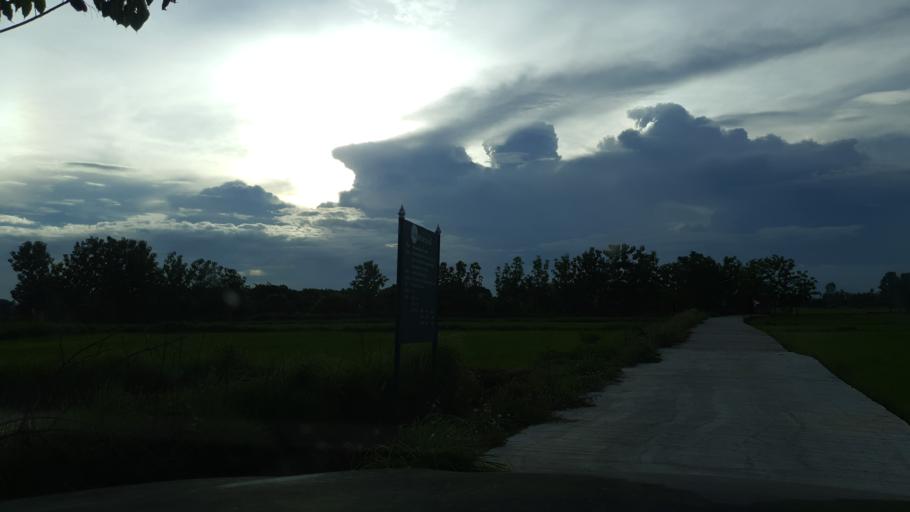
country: TH
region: Lamphun
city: Ban Thi
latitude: 18.6434
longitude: 99.1050
